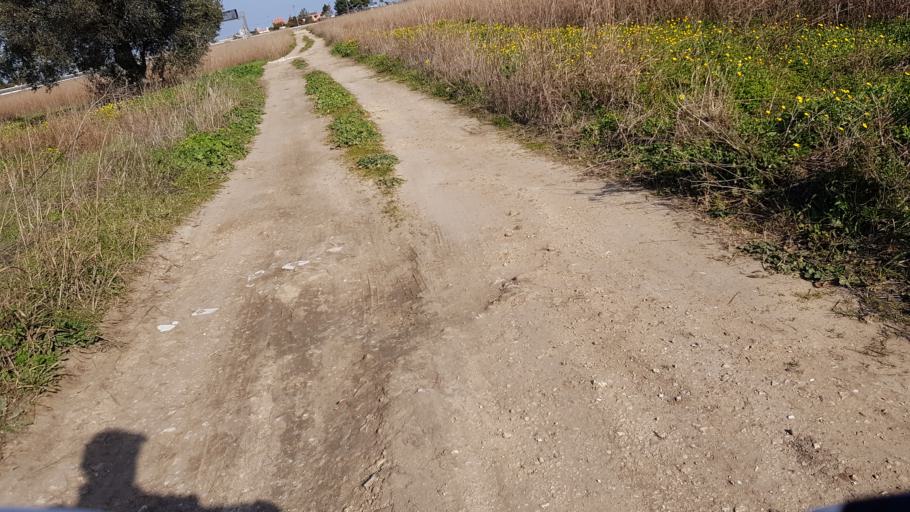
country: IT
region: Apulia
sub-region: Provincia di Brindisi
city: Brindisi
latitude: 40.6125
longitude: 17.8989
